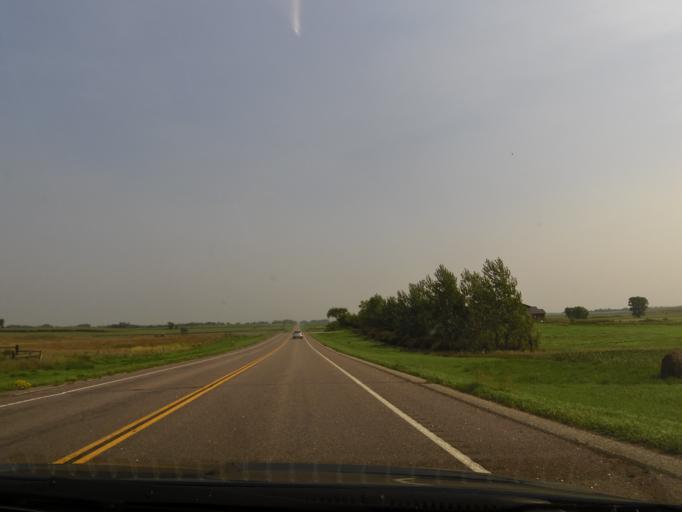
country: US
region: South Dakota
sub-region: Roberts County
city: Sisseton
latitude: 45.8484
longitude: -96.9495
